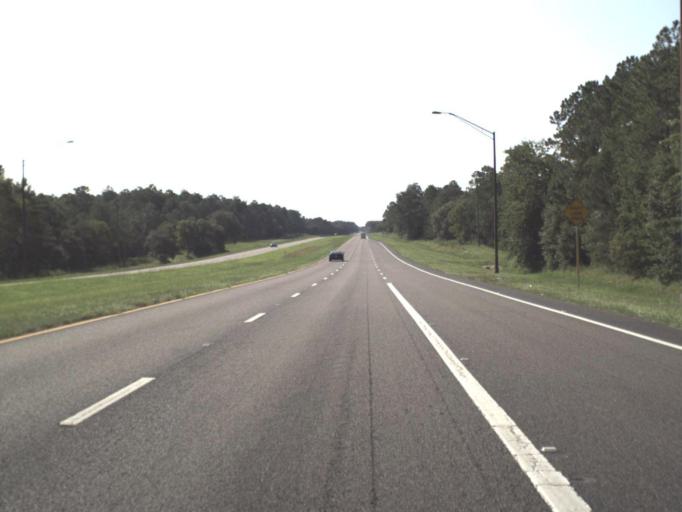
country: US
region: Florida
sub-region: Citrus County
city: Sugarmill Woods
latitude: 28.6830
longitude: -82.4926
